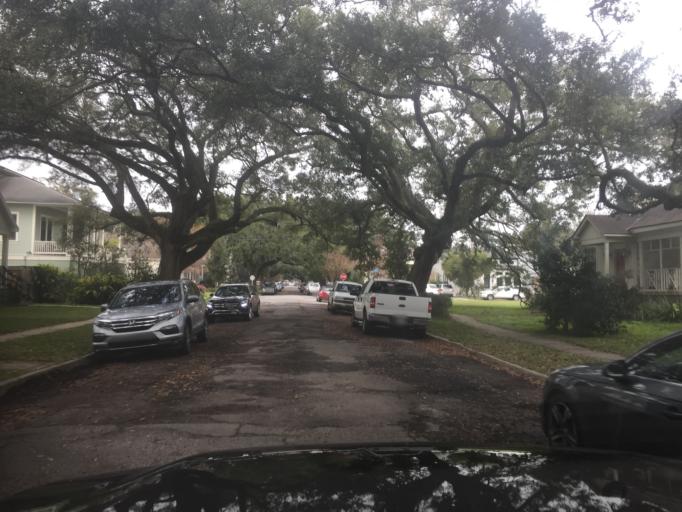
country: US
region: Louisiana
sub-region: Jefferson Parish
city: Metairie
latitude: 29.9984
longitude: -90.1065
